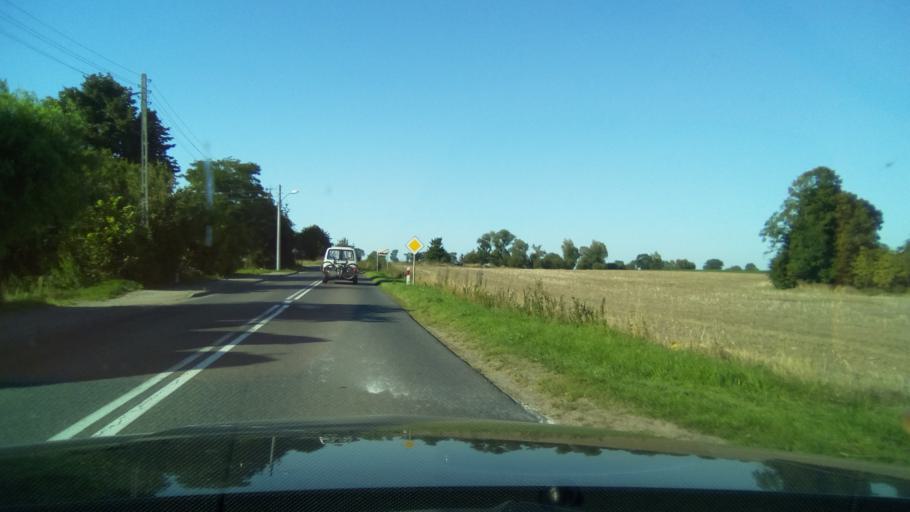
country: PL
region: West Pomeranian Voivodeship
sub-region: Powiat kamienski
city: Golczewo
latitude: 53.8293
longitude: 14.8925
